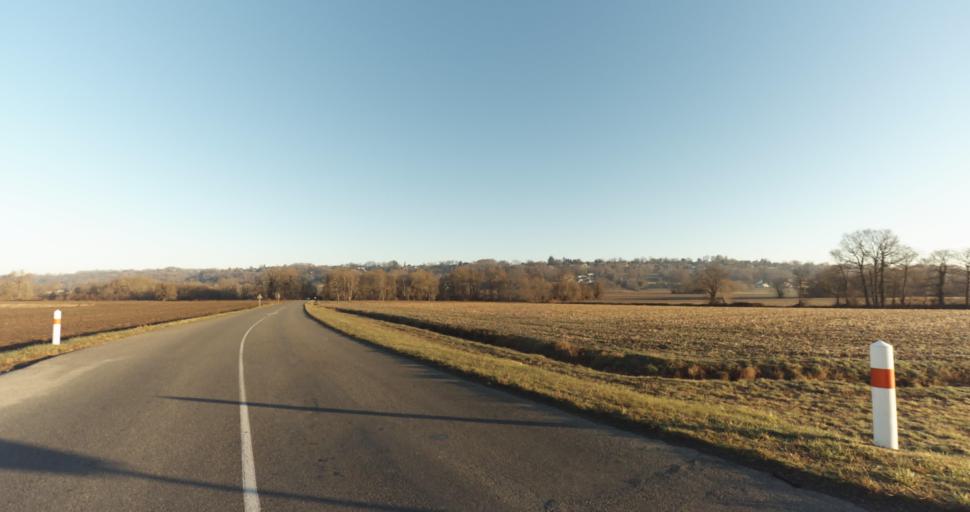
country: FR
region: Aquitaine
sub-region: Departement des Pyrenees-Atlantiques
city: Morlaas
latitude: 43.3170
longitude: -0.2750
